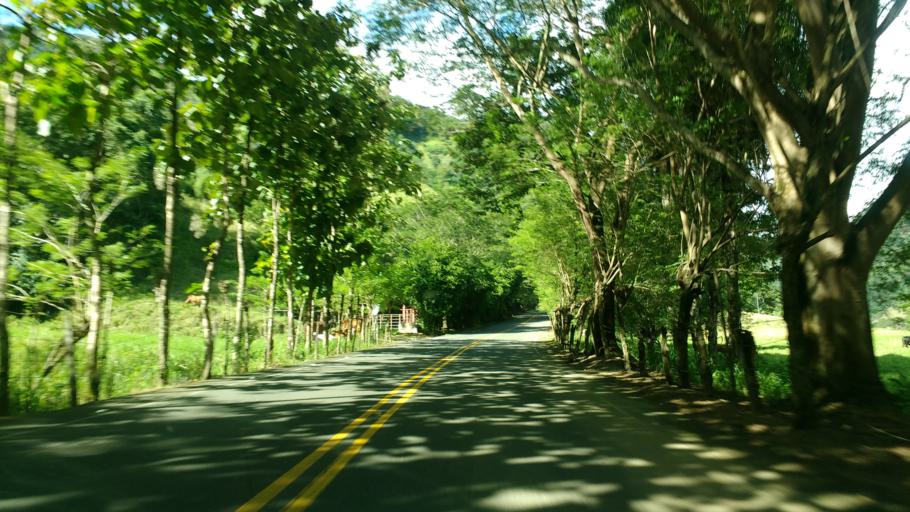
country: CO
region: Antioquia
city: Concordia
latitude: 6.0774
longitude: -75.8610
